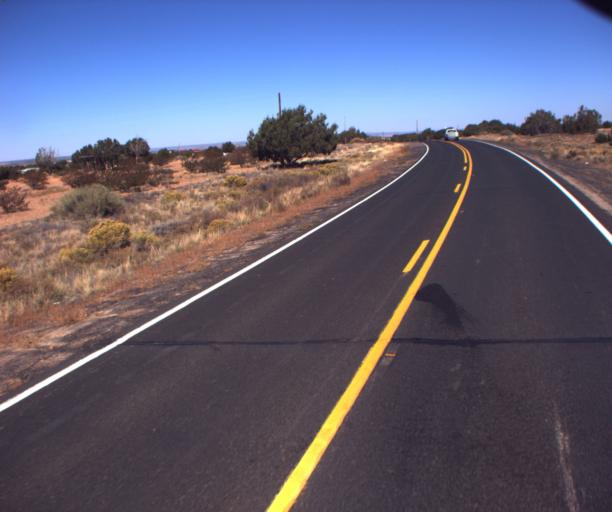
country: US
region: Arizona
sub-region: Navajo County
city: First Mesa
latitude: 35.8371
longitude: -110.5270
